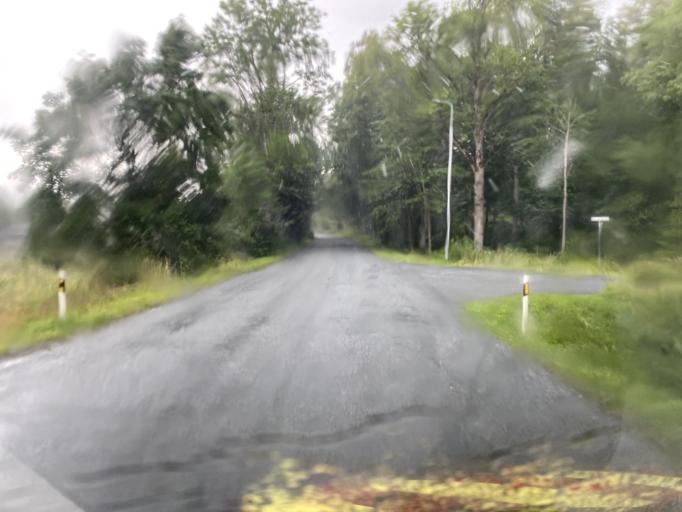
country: EE
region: Valgamaa
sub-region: Torva linn
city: Torva
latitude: 58.1482
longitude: 25.8043
